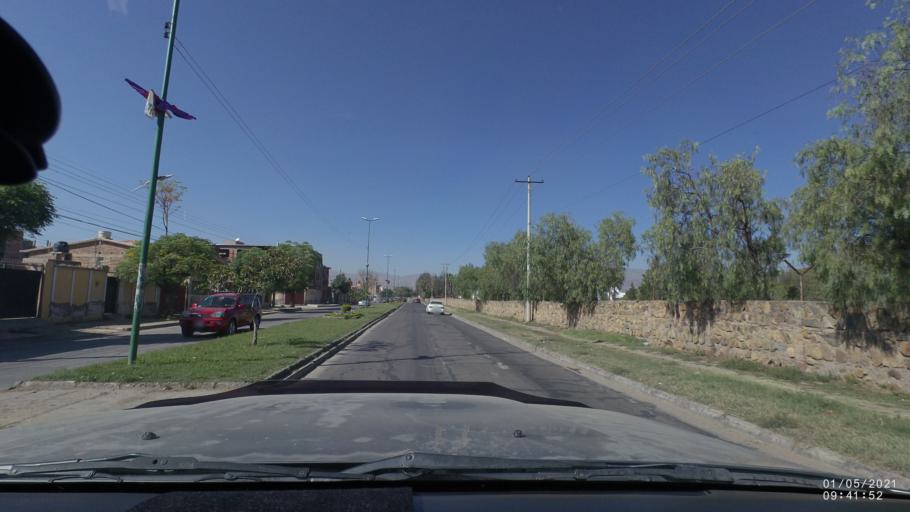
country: BO
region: Cochabamba
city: Cochabamba
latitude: -17.4234
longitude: -66.1670
